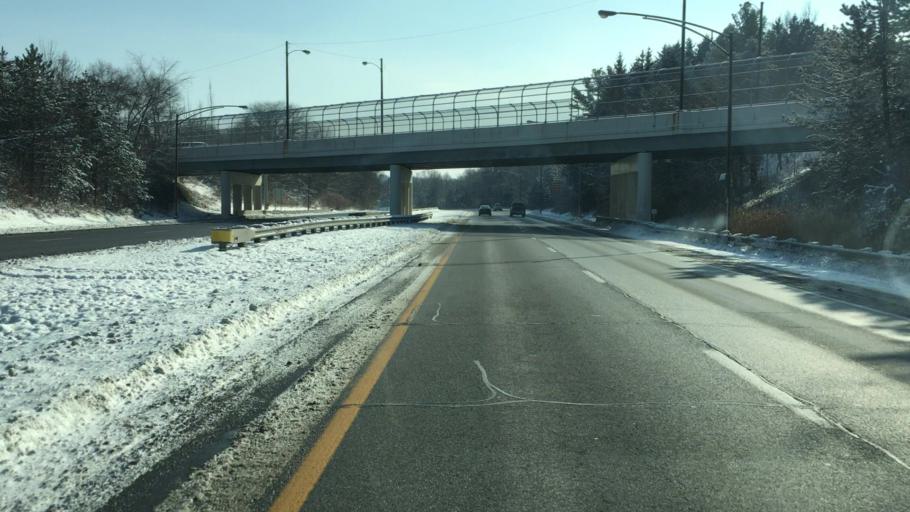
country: US
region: Ohio
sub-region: Mahoning County
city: Youngstown
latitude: 41.1080
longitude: -80.6879
